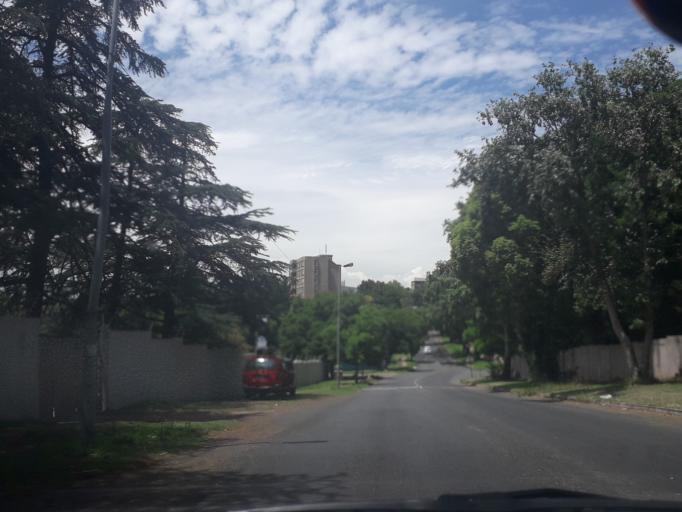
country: ZA
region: Gauteng
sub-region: City of Johannesburg Metropolitan Municipality
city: Johannesburg
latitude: -26.1200
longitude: 28.0798
